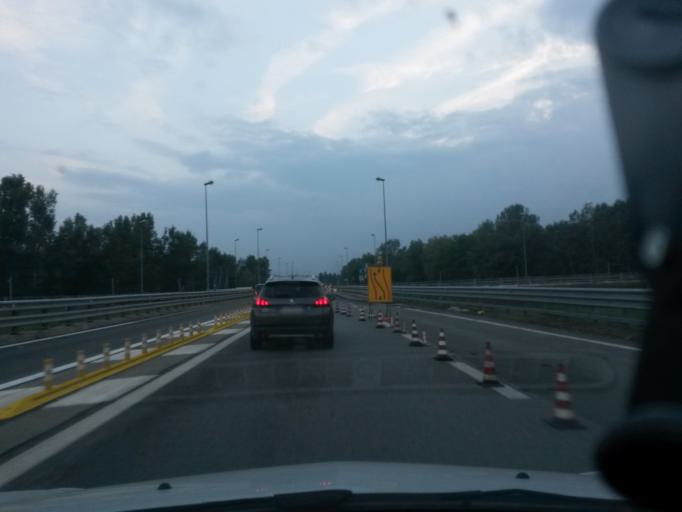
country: IT
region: Piedmont
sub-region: Provincia di Torino
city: Drubiaglio-Grangia
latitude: 45.0911
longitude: 7.4176
